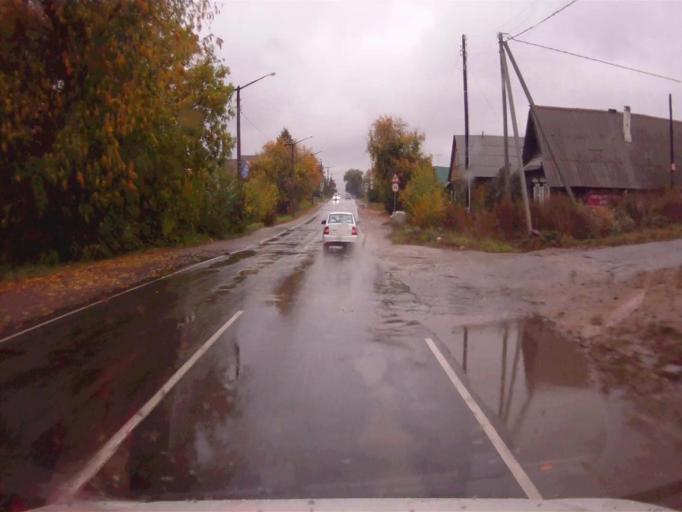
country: RU
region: Chelyabinsk
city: Kyshtym
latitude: 55.7216
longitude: 60.5347
